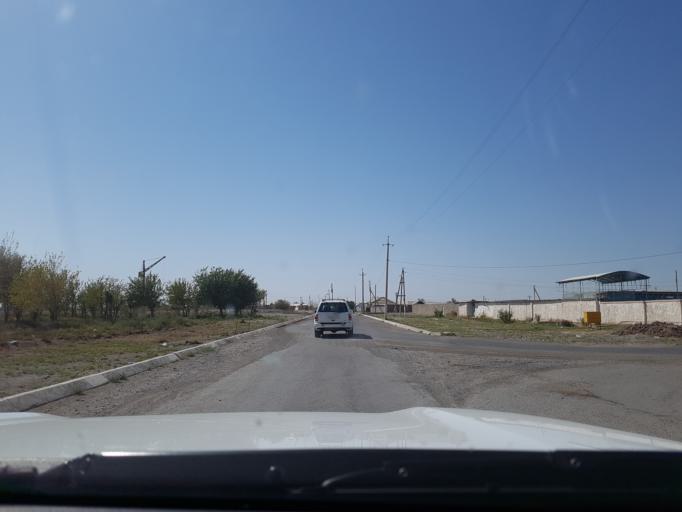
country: IR
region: Razavi Khorasan
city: Sarakhs
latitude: 36.5134
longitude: 61.2244
